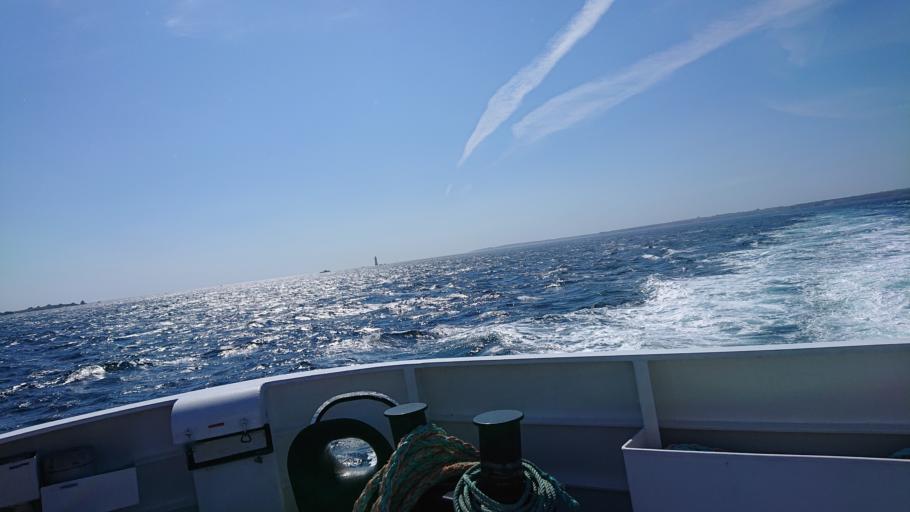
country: FR
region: Brittany
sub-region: Departement du Finistere
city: Lampaul-Plouarzel
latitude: 48.4438
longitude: -4.9888
